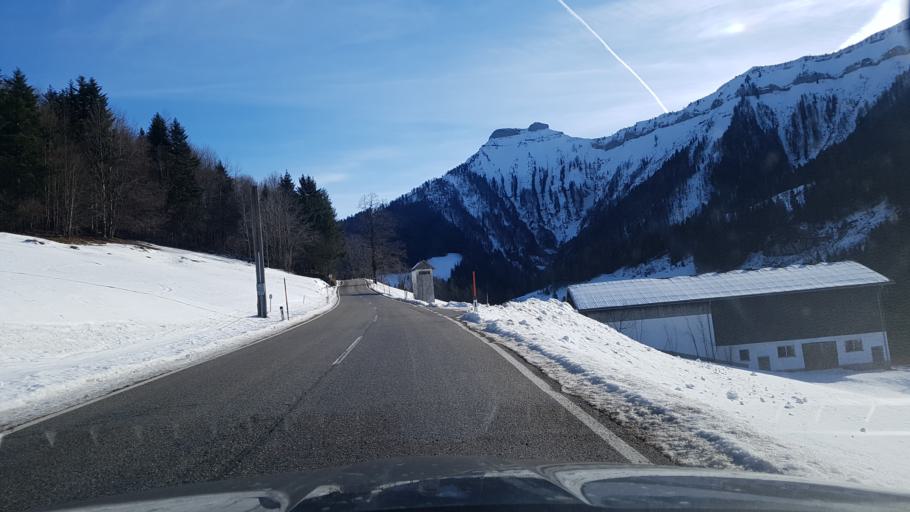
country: AT
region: Salzburg
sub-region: Politischer Bezirk Hallein
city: Krispl
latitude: 47.7036
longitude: 13.2098
